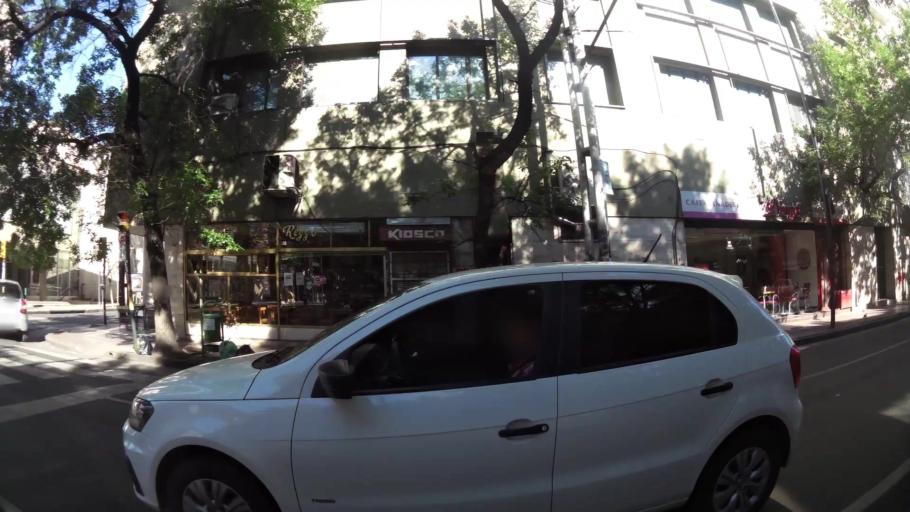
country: AR
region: Cordoba
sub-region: Departamento de Capital
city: Cordoba
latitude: -31.4115
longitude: -64.1852
